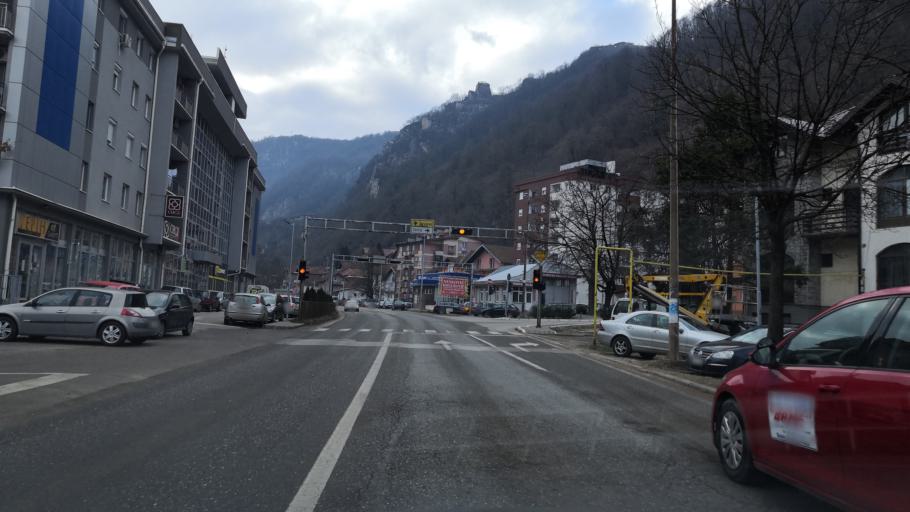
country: BA
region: Republika Srpska
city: Zvornik
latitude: 44.3797
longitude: 19.1032
